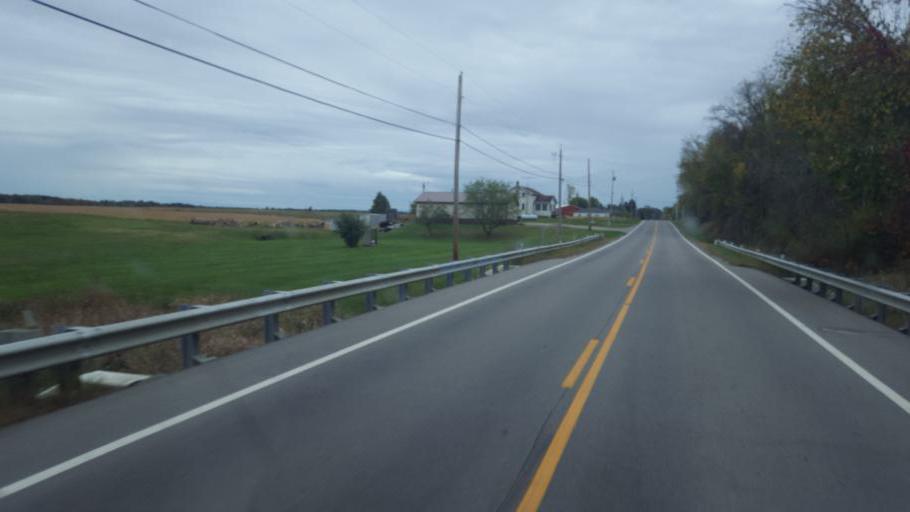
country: US
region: Ohio
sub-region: Huron County
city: New London
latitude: 41.1328
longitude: -82.4094
